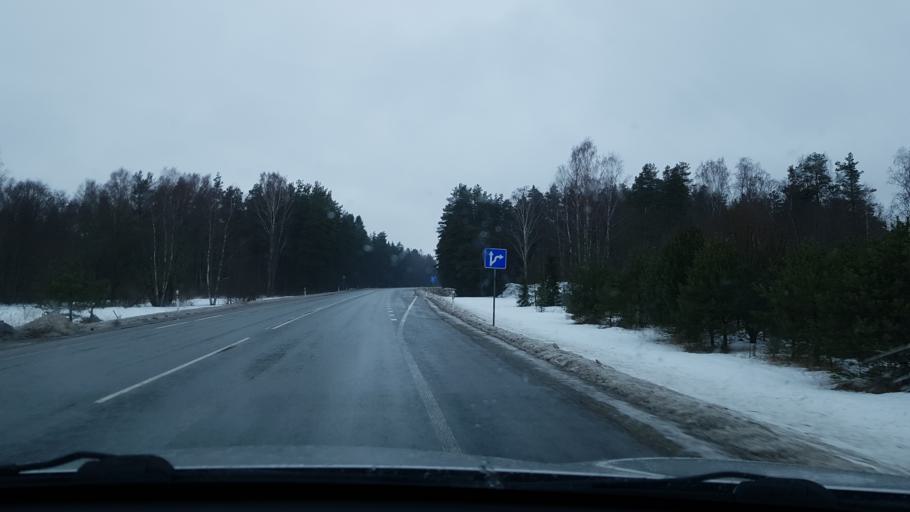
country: EE
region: Raplamaa
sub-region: Kohila vald
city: Kohila
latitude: 59.1619
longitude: 24.7727
